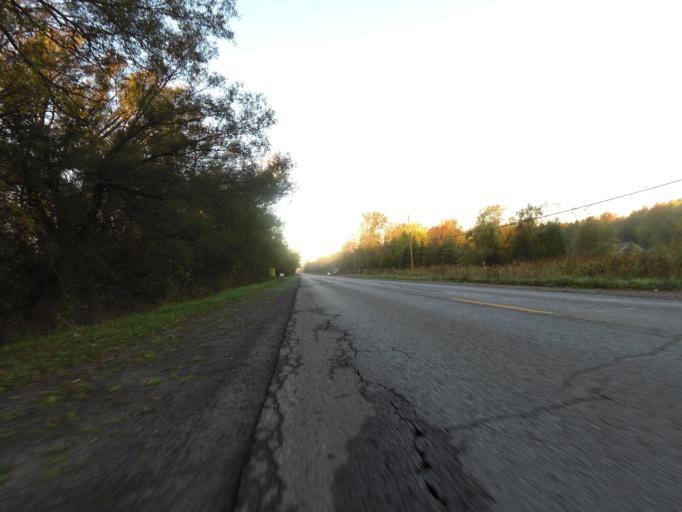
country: CA
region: Ontario
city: Quinte West
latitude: 44.0400
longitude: -77.6309
